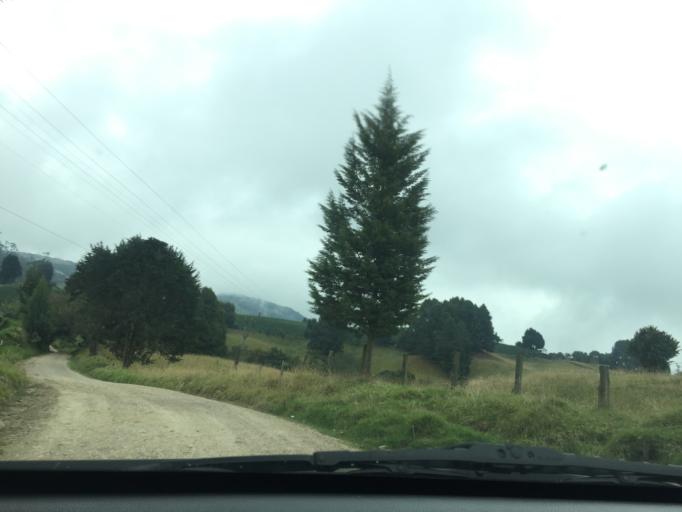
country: CO
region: Cundinamarca
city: El Rosal
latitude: 4.8902
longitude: -74.2583
